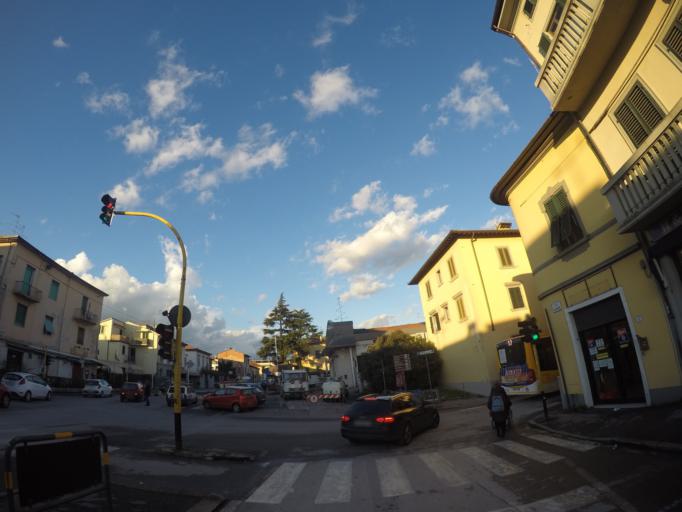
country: IT
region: Tuscany
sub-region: Provincia di Prato
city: Prato
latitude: 43.8828
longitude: 11.0913
